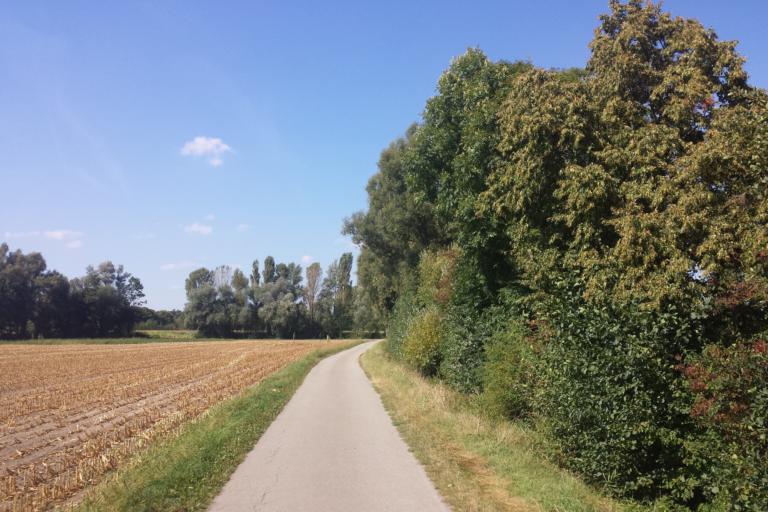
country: DE
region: Hesse
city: Lorsch
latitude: 49.6252
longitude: 8.5832
